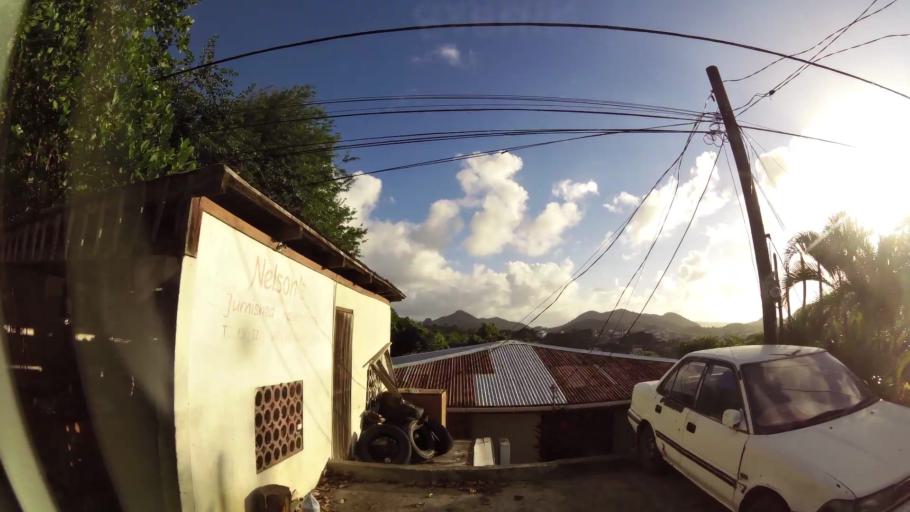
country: LC
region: Gros-Islet
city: Gros Islet
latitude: 14.0815
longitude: -60.9417
